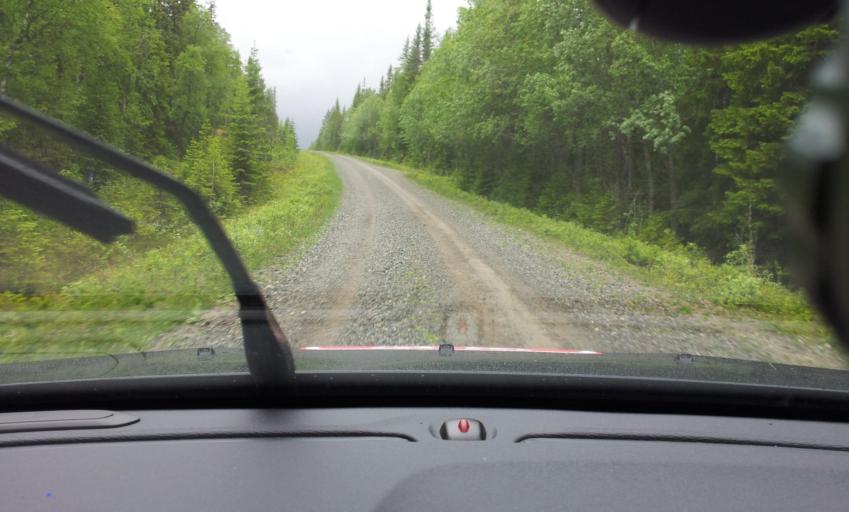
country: SE
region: Jaemtland
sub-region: Are Kommun
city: Jarpen
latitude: 63.2063
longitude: 13.2898
